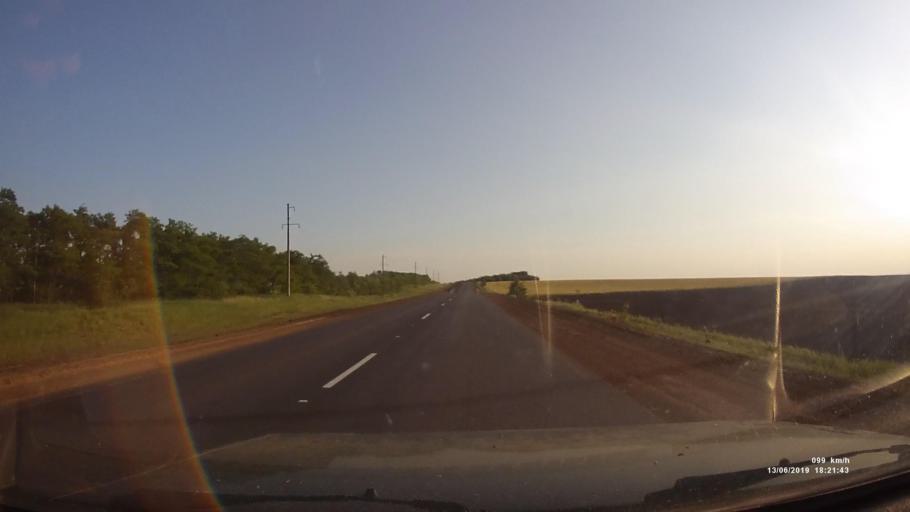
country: RU
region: Rostov
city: Kazanskaya
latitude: 49.8676
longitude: 41.2871
